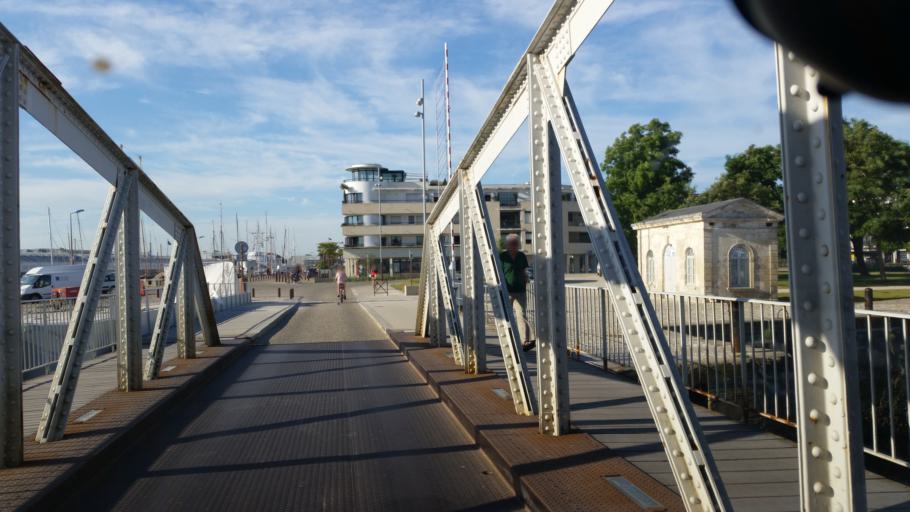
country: FR
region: Poitou-Charentes
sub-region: Departement de la Charente-Maritime
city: La Rochelle
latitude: 46.1546
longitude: -1.1527
